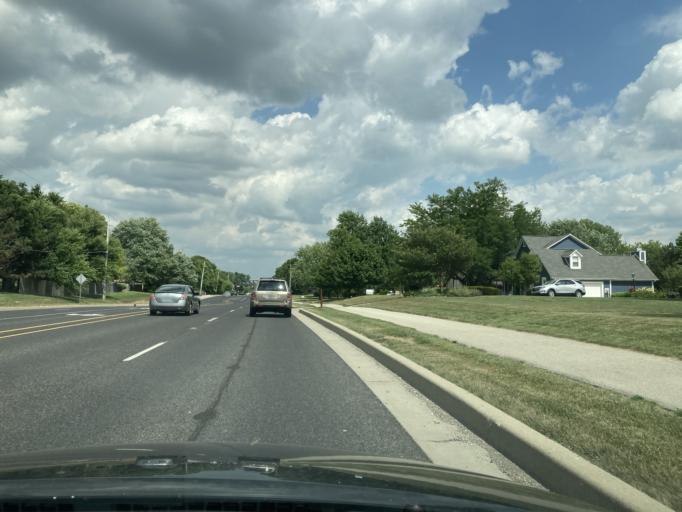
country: US
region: Indiana
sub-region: Hamilton County
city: Carmel
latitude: 39.9998
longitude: -86.1414
